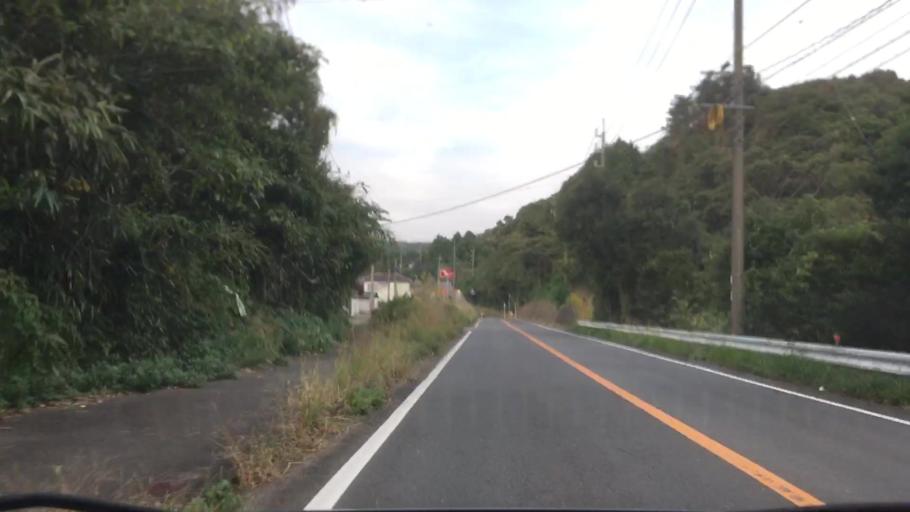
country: JP
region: Nagasaki
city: Togitsu
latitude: 32.9436
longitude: 129.6582
